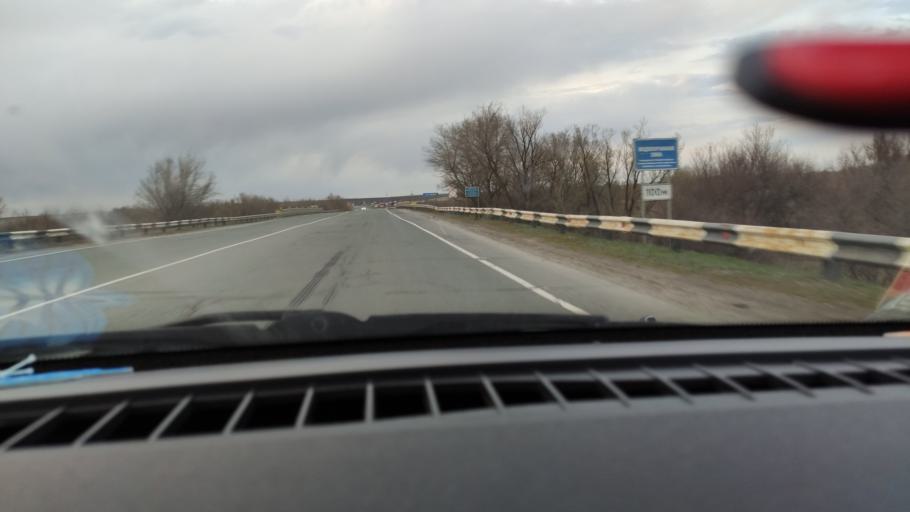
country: RU
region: Saratov
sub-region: Saratovskiy Rayon
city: Saratov
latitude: 51.7277
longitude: 46.0310
